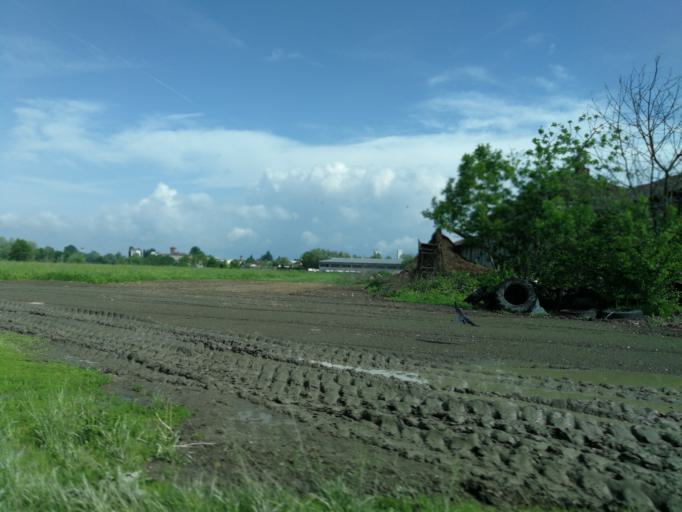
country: IT
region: Piedmont
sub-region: Provincia di Cuneo
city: Faule
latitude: 44.8079
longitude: 7.5820
